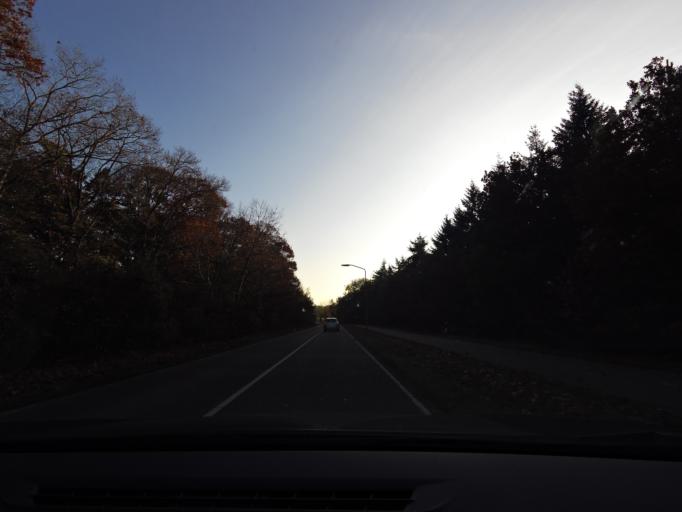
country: NL
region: North Brabant
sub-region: Gemeente Breda
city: Breda
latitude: 51.5269
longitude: 4.7695
